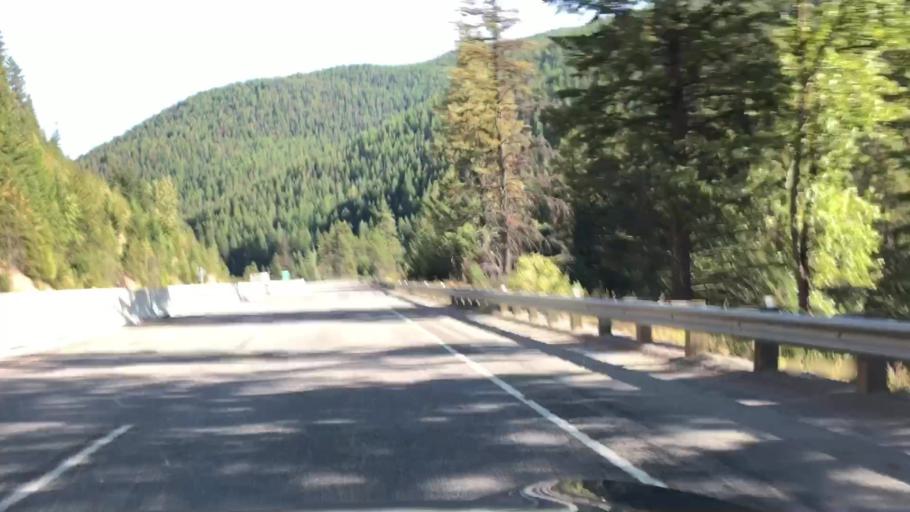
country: US
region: Montana
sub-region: Sanders County
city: Thompson Falls
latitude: 47.3970
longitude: -115.4563
